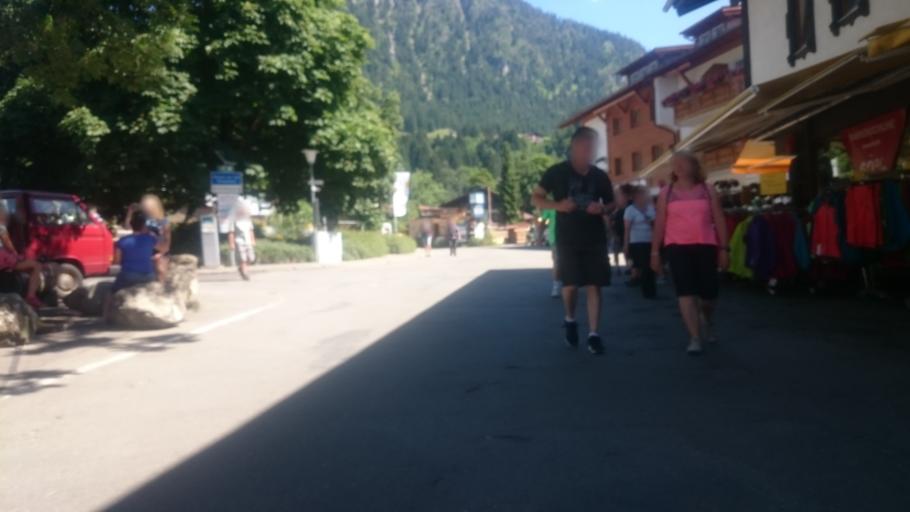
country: DE
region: Bavaria
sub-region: Swabia
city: Oberstdorf
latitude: 47.4048
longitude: 10.2843
